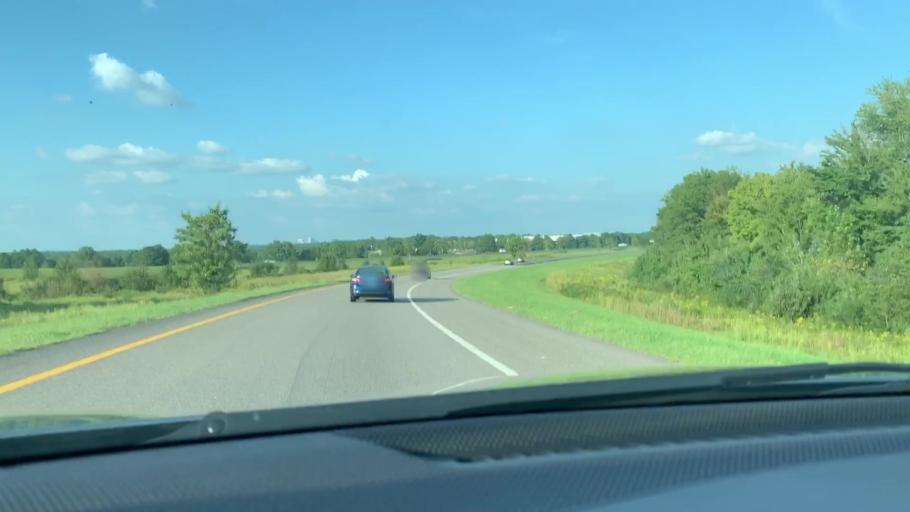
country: US
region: South Carolina
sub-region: Lexington County
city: Pineridge
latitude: 33.9248
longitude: -81.0673
